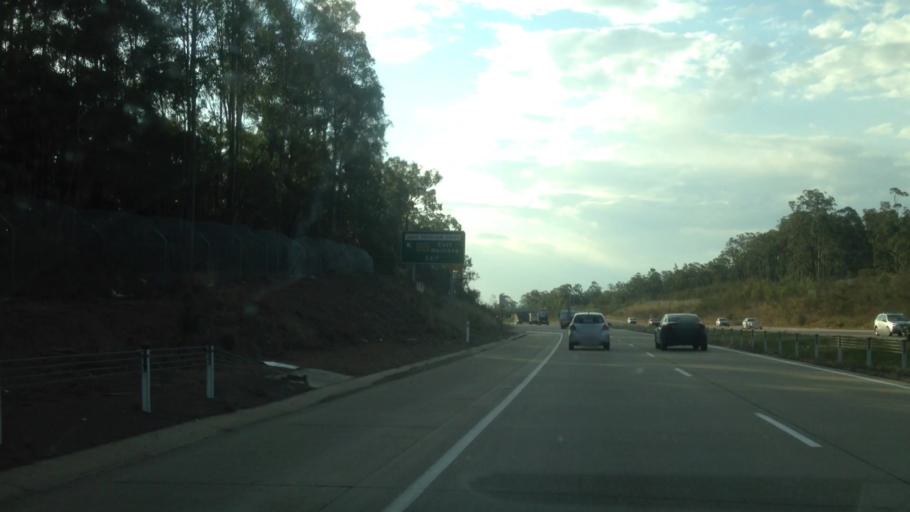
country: AU
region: New South Wales
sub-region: Cessnock
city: Heddon Greta
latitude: -32.8336
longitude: 151.5364
